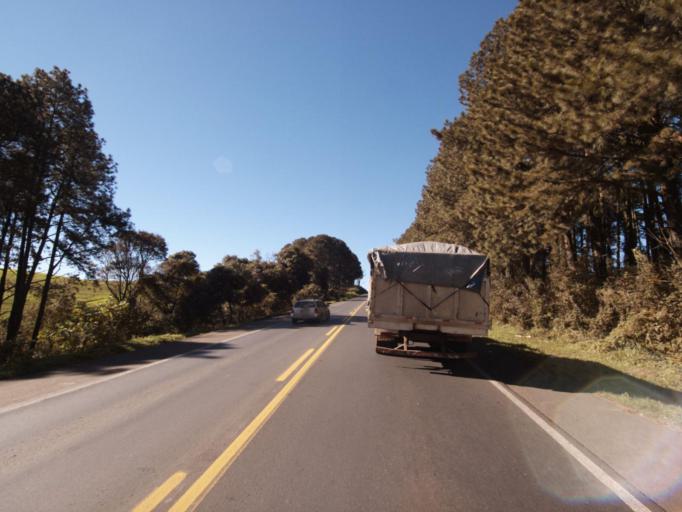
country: BR
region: Santa Catarina
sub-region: Xanxere
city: Xanxere
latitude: -26.9104
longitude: -52.4716
